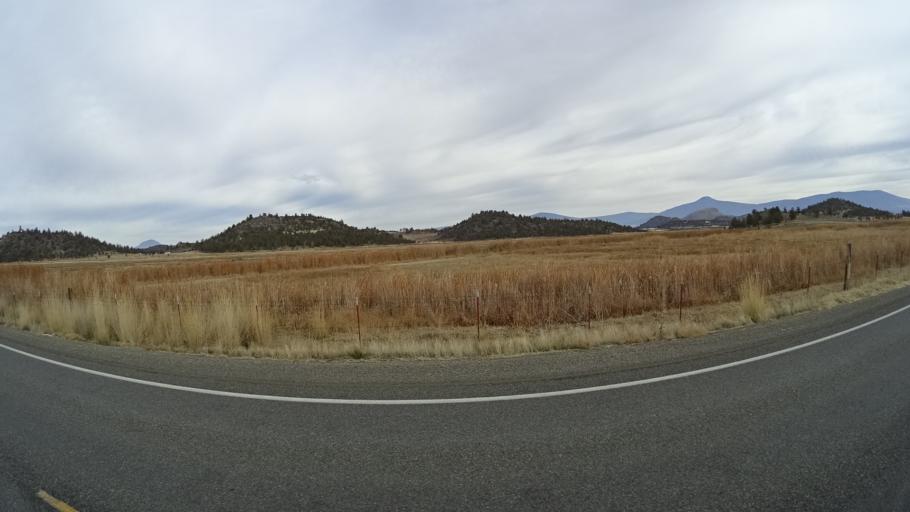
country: US
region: California
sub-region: Siskiyou County
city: Montague
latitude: 41.6456
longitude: -122.4922
